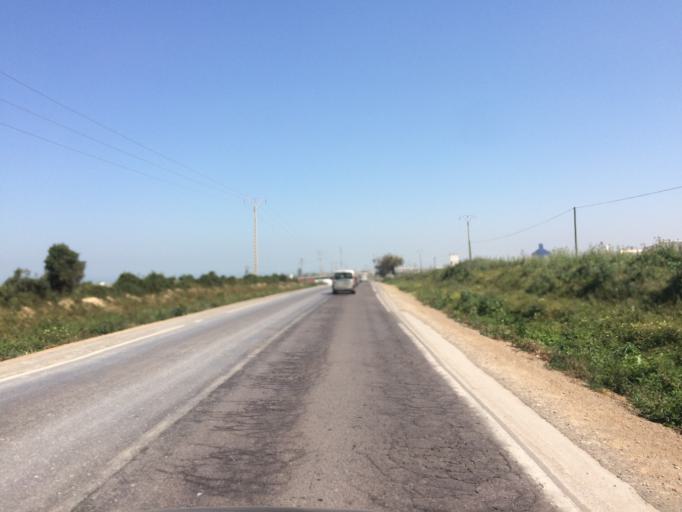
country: MA
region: Doukkala-Abda
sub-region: El-Jadida
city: Moulay Abdallah
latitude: 33.1725
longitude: -8.6011
